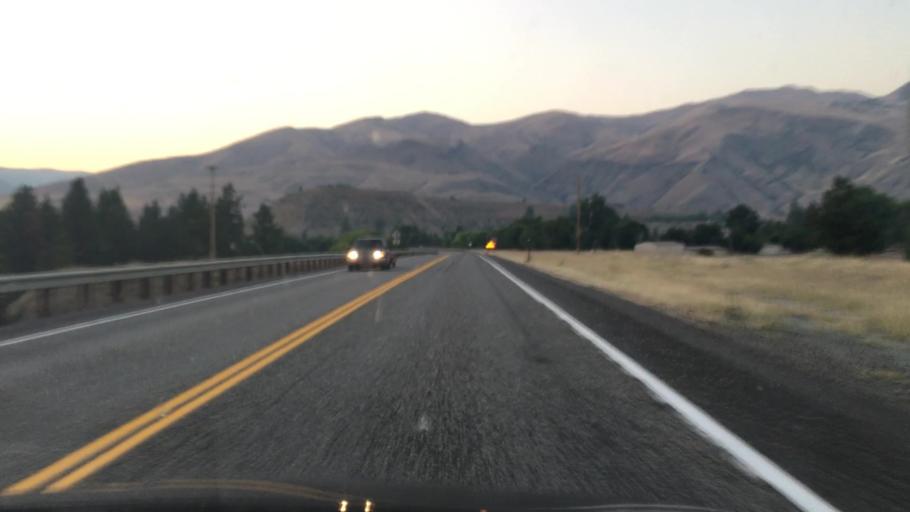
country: US
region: Idaho
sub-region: Idaho County
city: Grangeville
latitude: 45.6575
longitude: -116.2909
